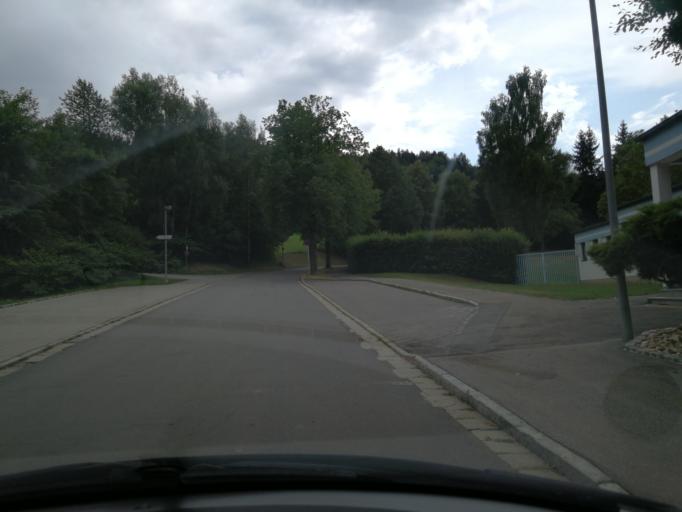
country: DE
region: Bavaria
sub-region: Upper Palatinate
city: Falkenstein
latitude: 49.0988
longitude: 12.4785
